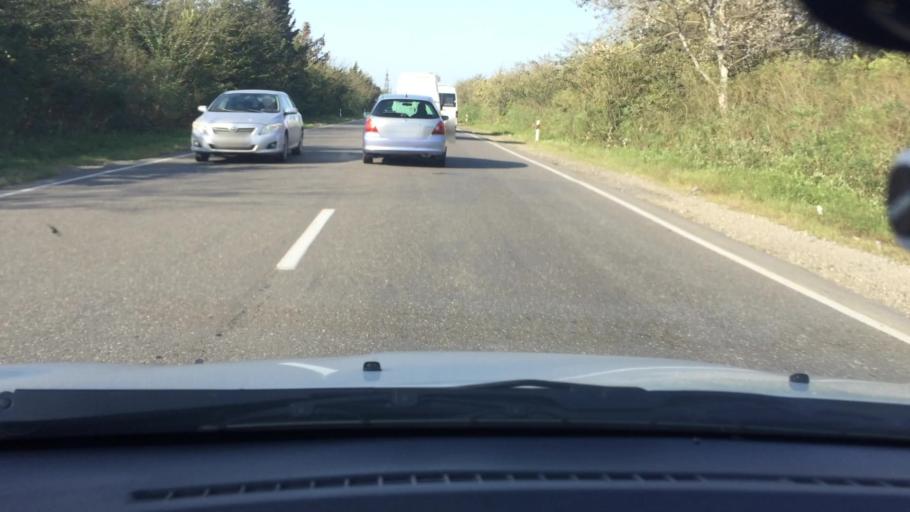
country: GE
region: Imereti
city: Vani
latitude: 42.1940
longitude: 42.5063
